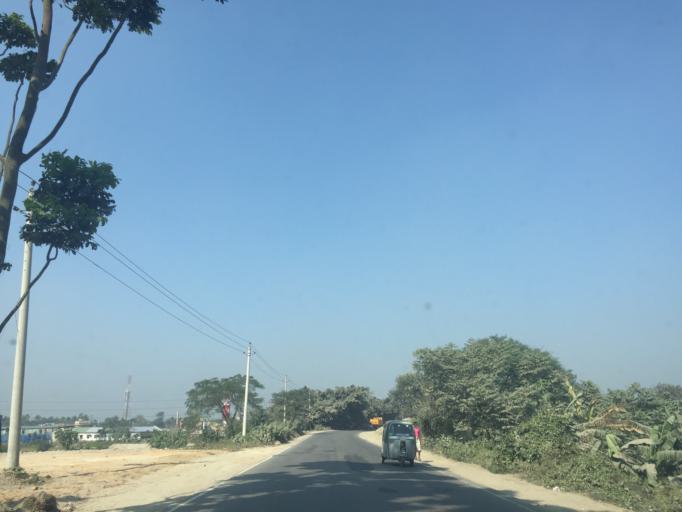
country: BD
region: Dhaka
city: Tungi
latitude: 23.8456
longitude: 90.3409
